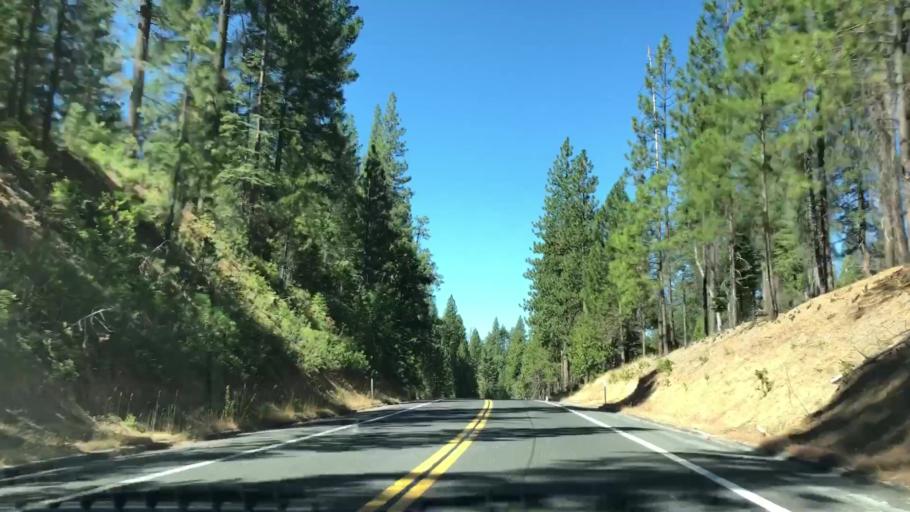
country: US
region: California
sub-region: Mariposa County
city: Midpines
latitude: 37.8135
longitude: -119.8911
